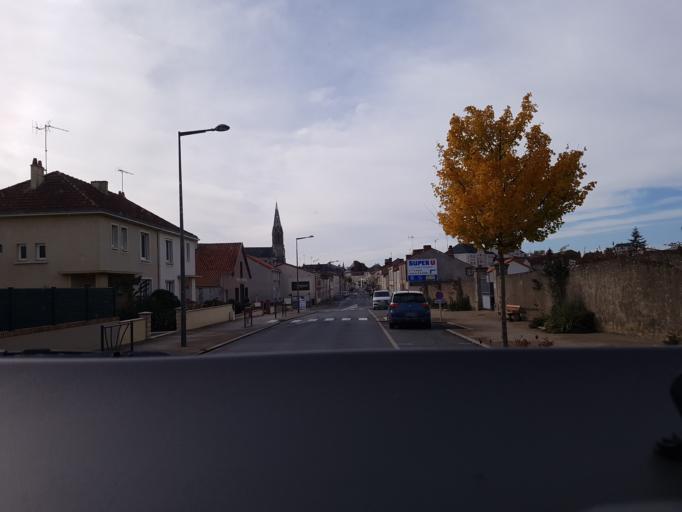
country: FR
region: Pays de la Loire
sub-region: Departement de Maine-et-Loire
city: Beaupreau
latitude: 47.2047
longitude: -0.9790
